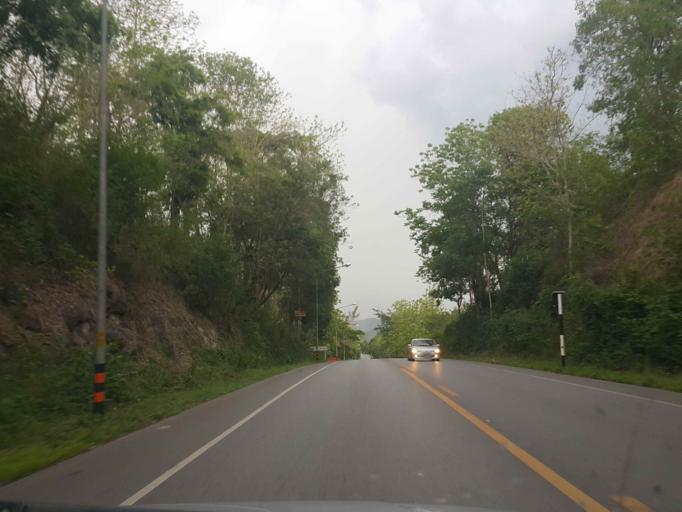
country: TH
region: Phrae
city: Den Chai
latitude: 17.9729
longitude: 100.0429
